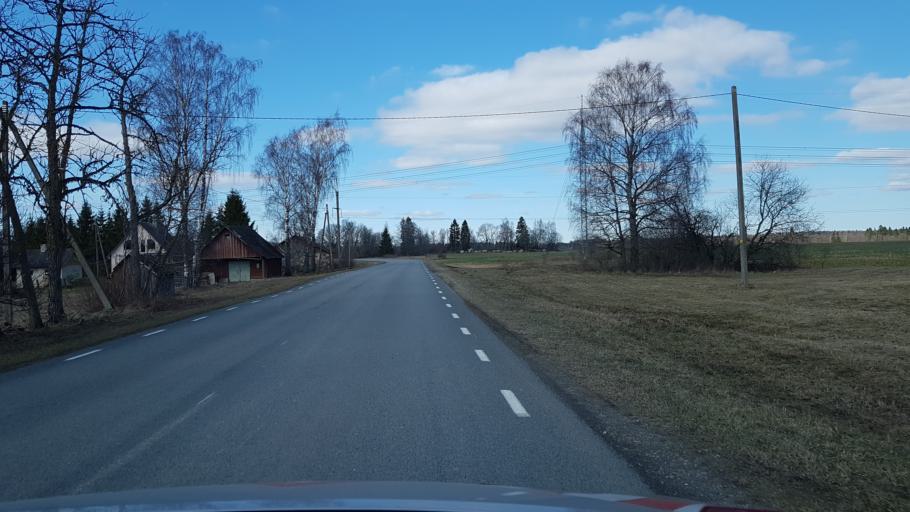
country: EE
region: Laeaene-Virumaa
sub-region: Tamsalu vald
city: Tamsalu
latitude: 59.1772
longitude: 26.0531
